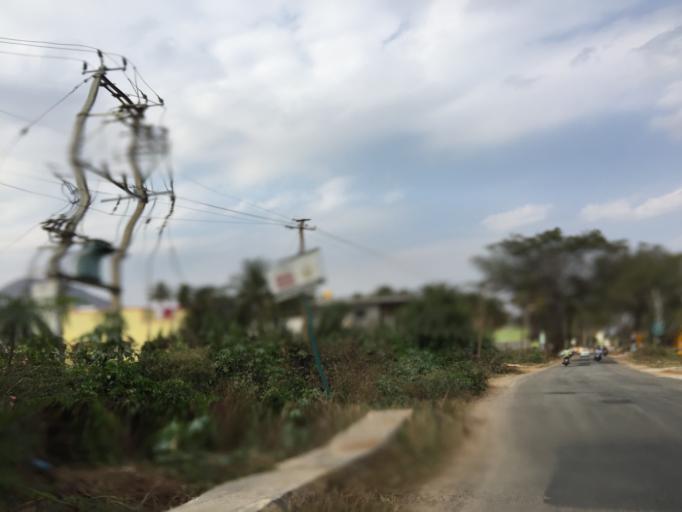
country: IN
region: Karnataka
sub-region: Chikkaballapur
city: Chik Ballapur
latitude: 13.3891
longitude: 77.6991
